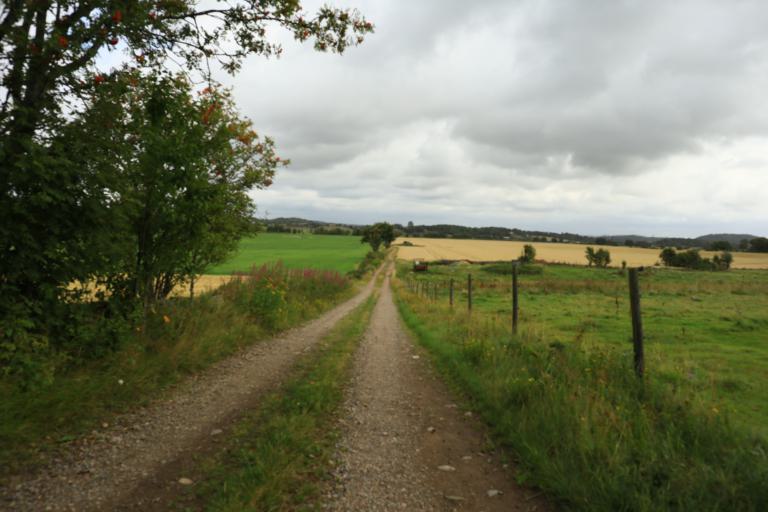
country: SE
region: Halland
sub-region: Varbergs Kommun
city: Traslovslage
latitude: 57.1212
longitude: 12.3239
